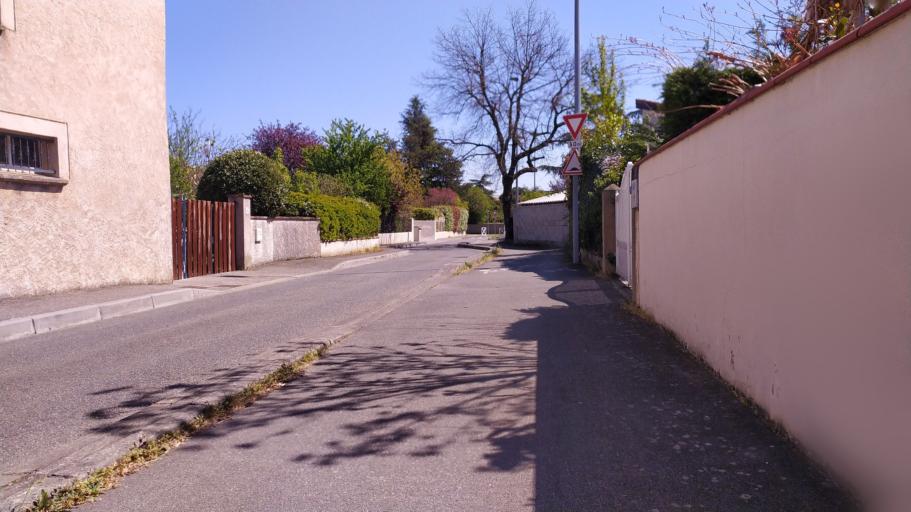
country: FR
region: Midi-Pyrenees
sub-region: Departement de la Haute-Garonne
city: Tournefeuille
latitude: 43.5871
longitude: 1.3177
